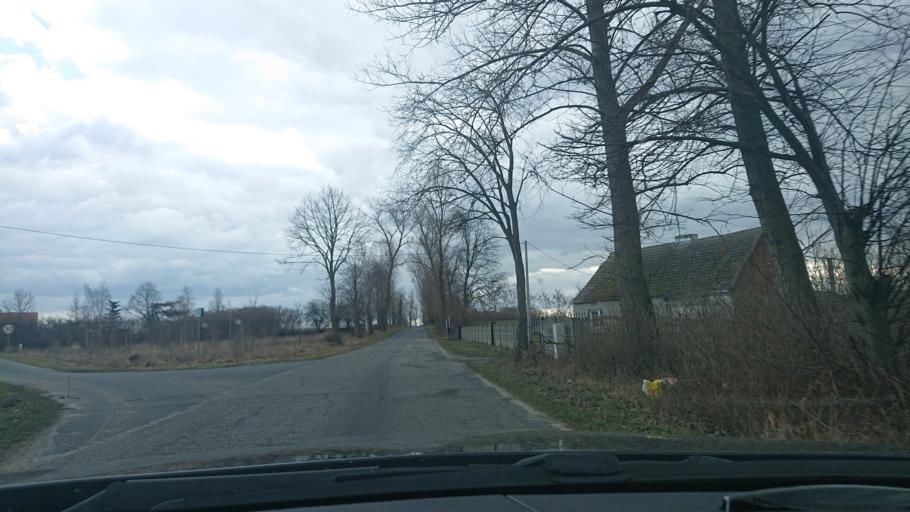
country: PL
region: Greater Poland Voivodeship
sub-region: Powiat gnieznienski
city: Gniezno
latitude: 52.5829
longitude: 17.6880
